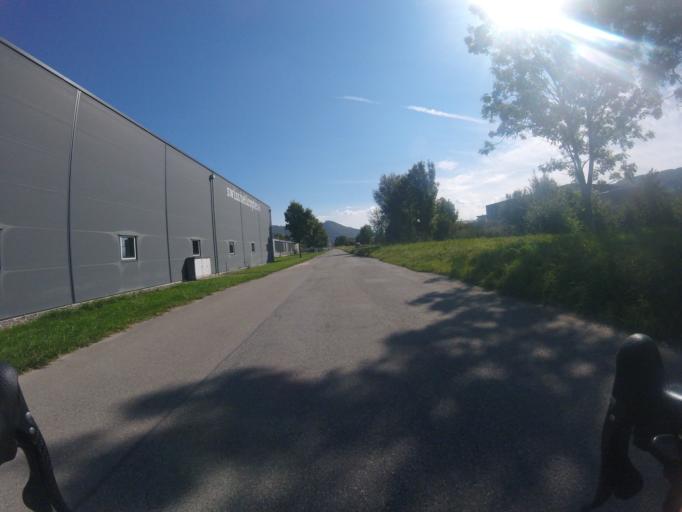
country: CH
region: Bern
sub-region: Bern-Mittelland District
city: Belp
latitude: 46.9065
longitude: 7.4972
